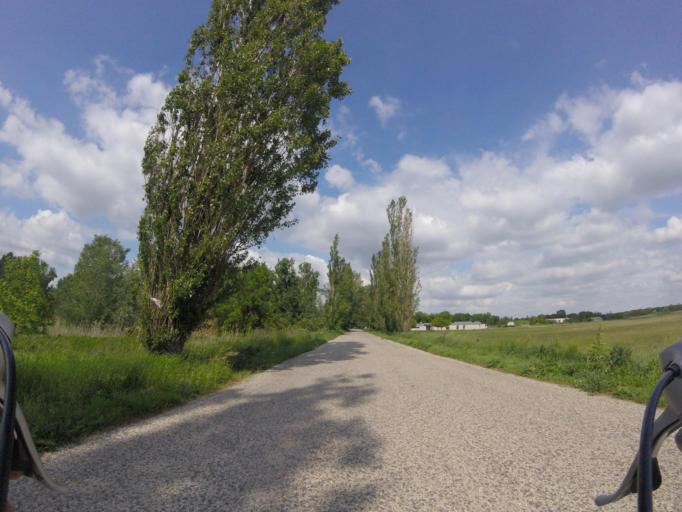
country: HU
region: Fejer
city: Szabadbattyan
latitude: 47.0887
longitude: 18.4183
